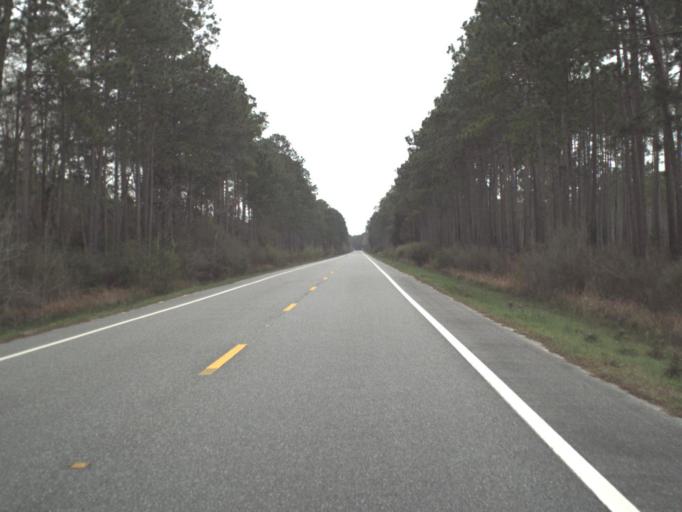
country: US
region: Florida
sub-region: Franklin County
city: Apalachicola
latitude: 29.8635
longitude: -84.9742
